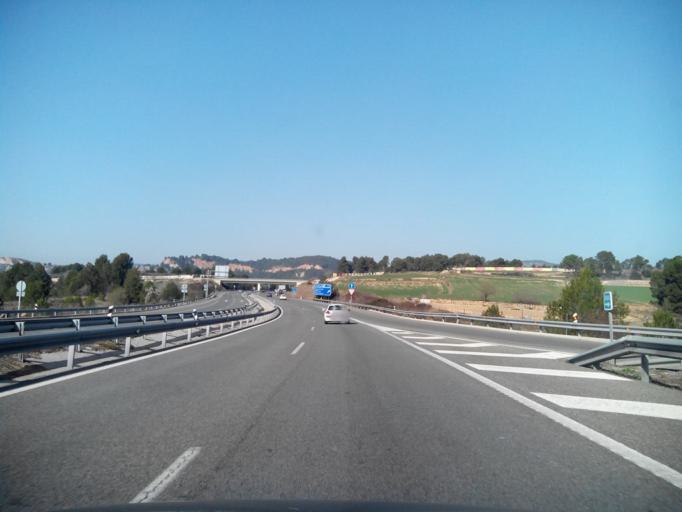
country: ES
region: Catalonia
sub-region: Provincia de Barcelona
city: Odena
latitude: 41.5939
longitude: 1.6484
